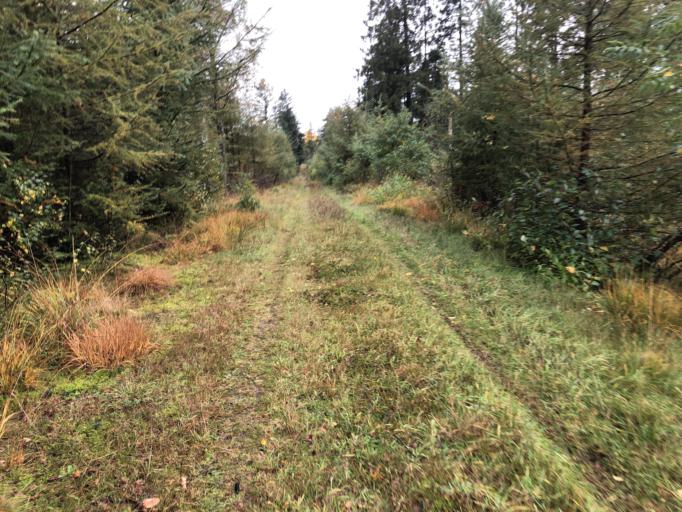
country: DK
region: Central Jutland
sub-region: Holstebro Kommune
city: Ulfborg
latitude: 56.2703
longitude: 8.4375
